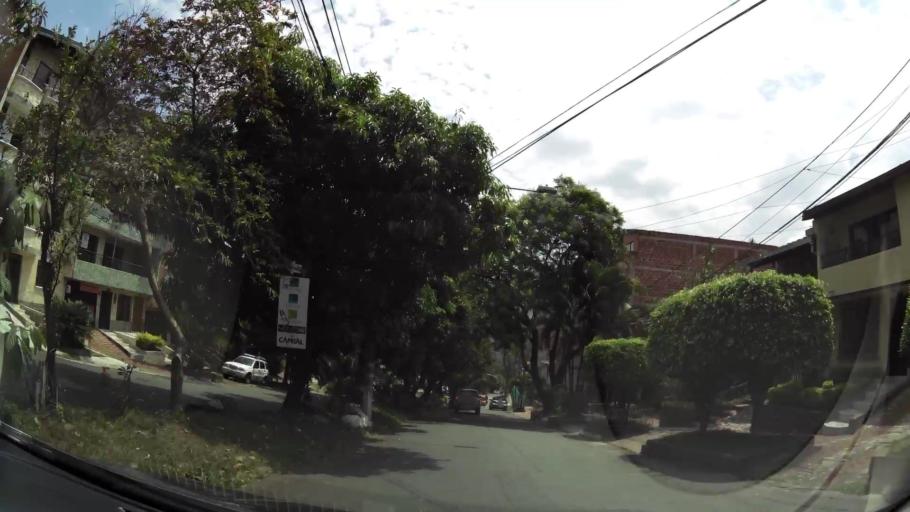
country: CO
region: Antioquia
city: Bello
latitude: 6.3170
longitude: -75.5627
